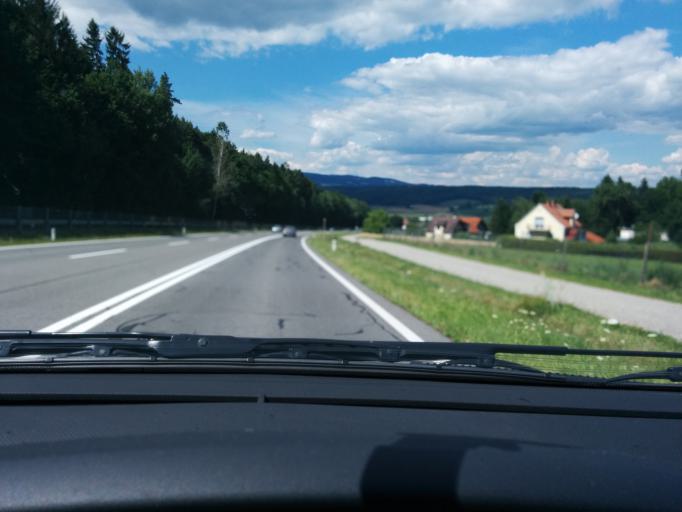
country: AT
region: Styria
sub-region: Politischer Bezirk Hartberg-Fuerstenfeld
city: Lafnitz
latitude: 47.3573
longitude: 16.0112
